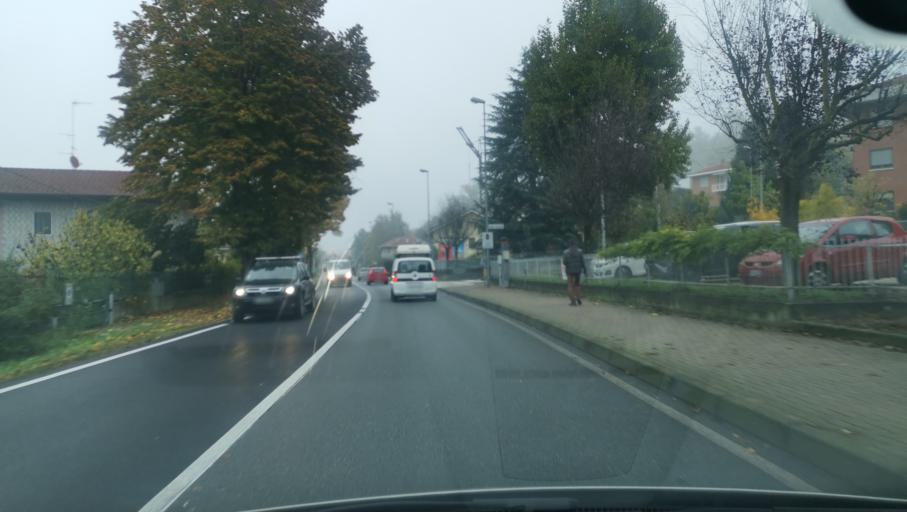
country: IT
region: Piedmont
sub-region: Provincia di Torino
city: Castiglione Torinese
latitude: 45.1194
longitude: 7.8093
